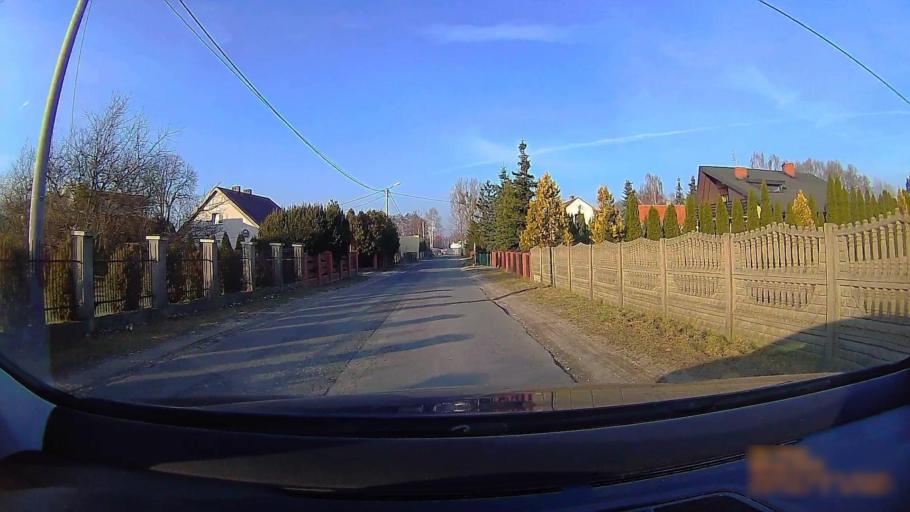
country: PL
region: Greater Poland Voivodeship
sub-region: Konin
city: Konin
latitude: 52.1891
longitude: 18.3324
